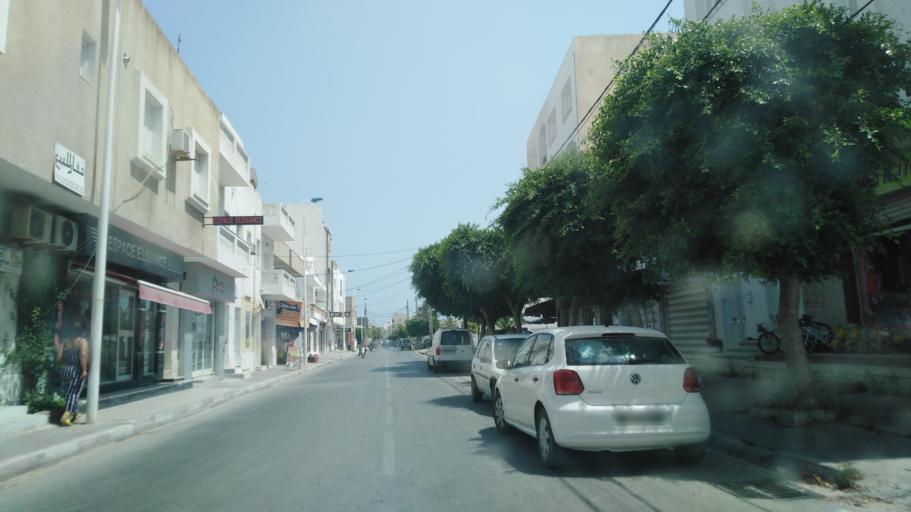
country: TN
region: Al Mahdiyah
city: Mahdia
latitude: 35.5117
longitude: 11.0477
